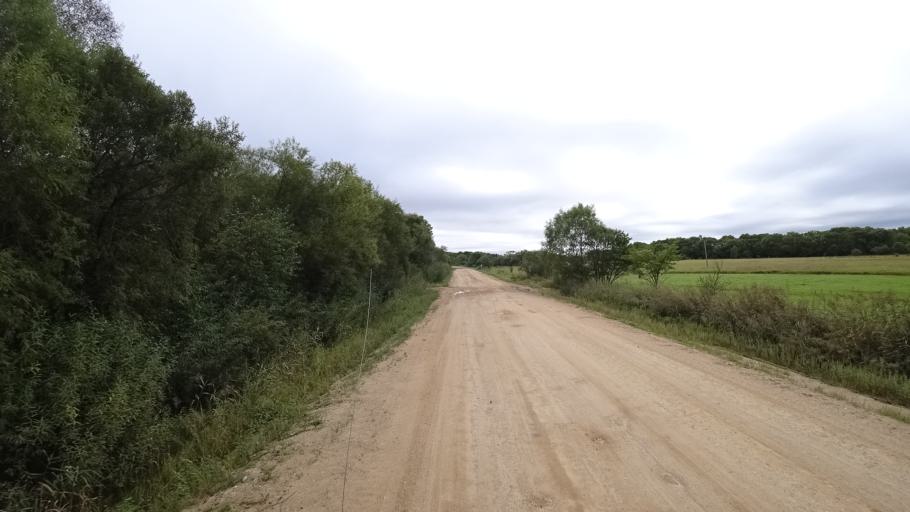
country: RU
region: Primorskiy
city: Monastyrishche
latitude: 44.1014
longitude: 132.6058
